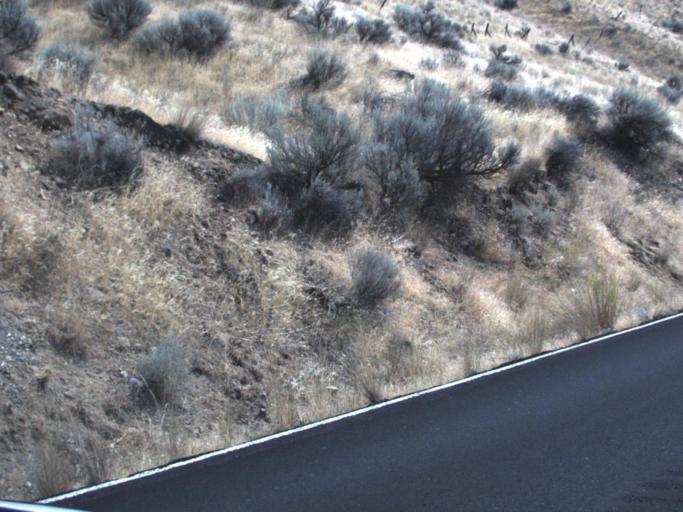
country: US
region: Washington
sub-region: Yakima County
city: Selah
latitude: 46.7880
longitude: -120.4504
